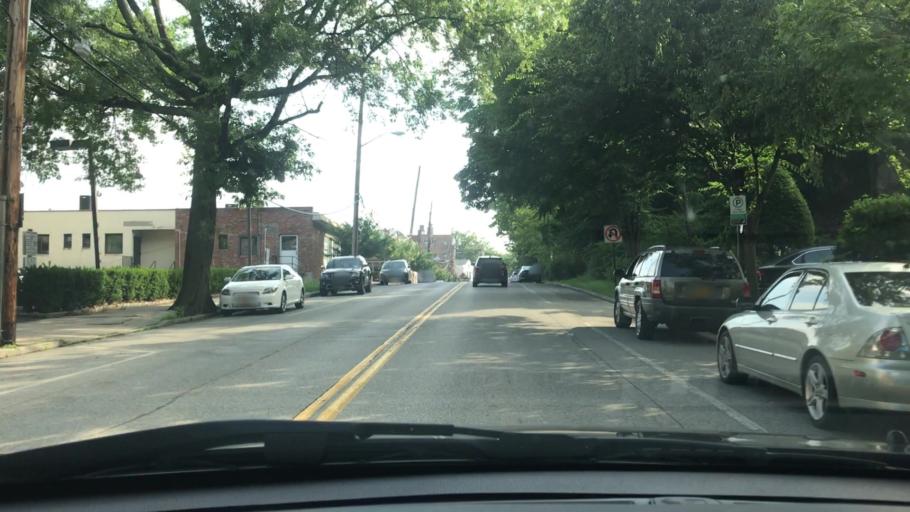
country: US
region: New York
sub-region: Westchester County
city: Larchmont
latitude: 40.9299
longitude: -73.7625
